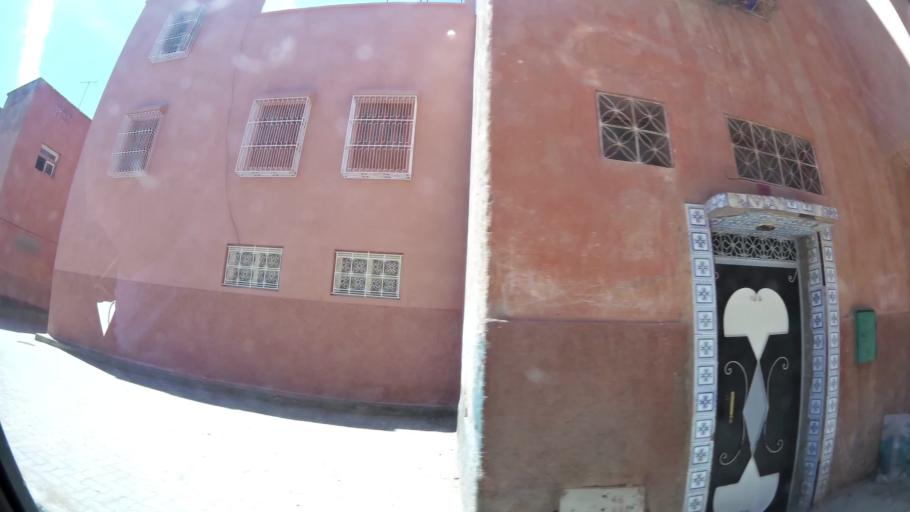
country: MA
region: Marrakech-Tensift-Al Haouz
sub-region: Marrakech
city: Marrakesh
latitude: 31.6574
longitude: -8.0016
